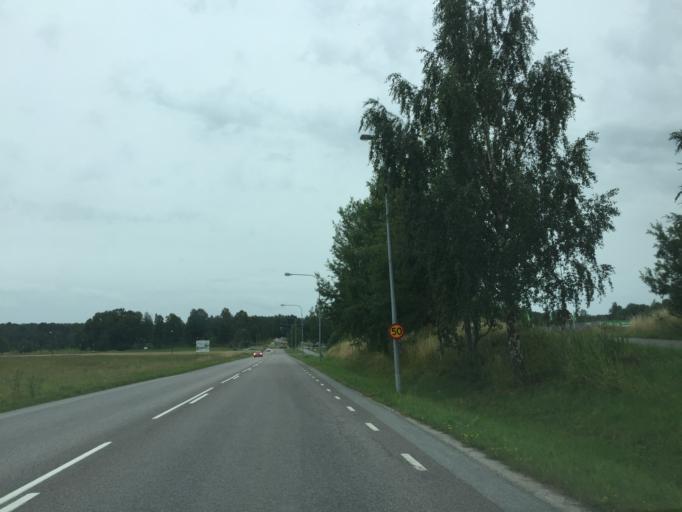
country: SE
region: OErebro
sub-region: Orebro Kommun
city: Orebro
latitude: 59.2543
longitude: 15.1968
